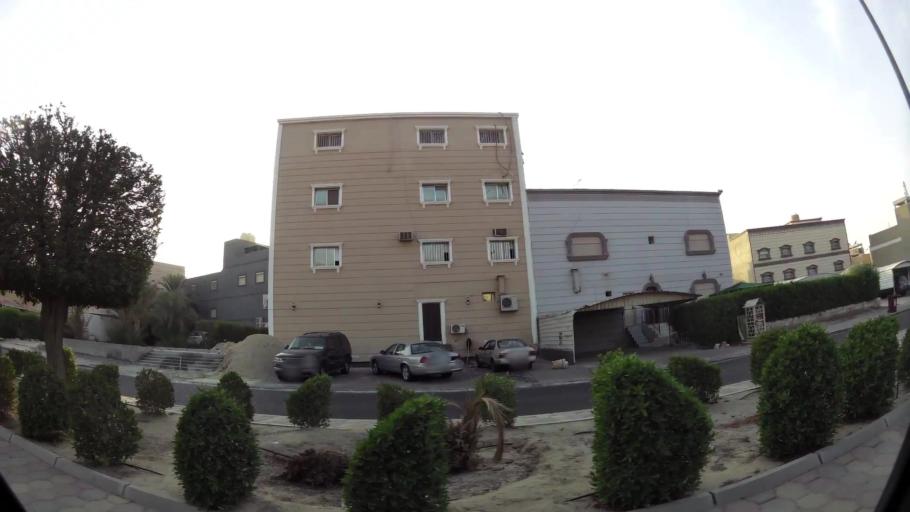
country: KW
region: Mubarak al Kabir
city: Sabah as Salim
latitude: 29.2530
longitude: 48.0712
